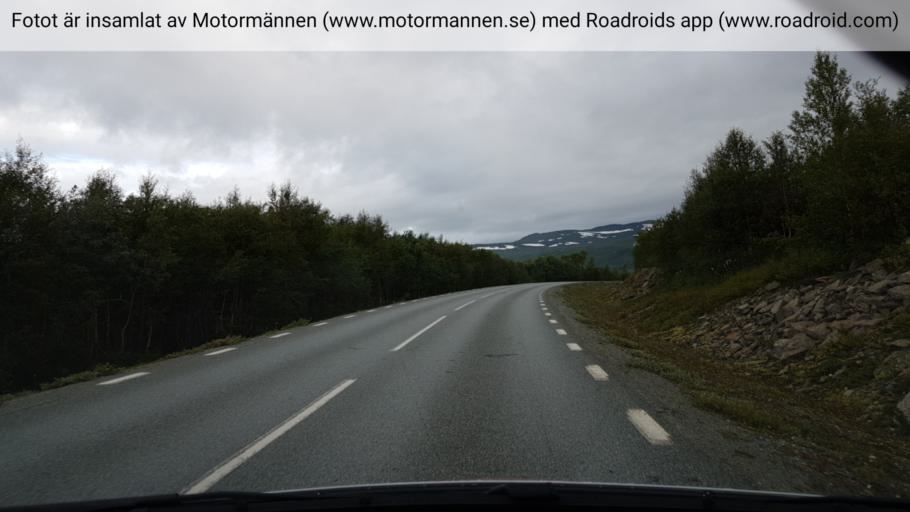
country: NO
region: Nordland
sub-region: Rana
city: Mo i Rana
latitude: 66.1021
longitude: 14.8237
